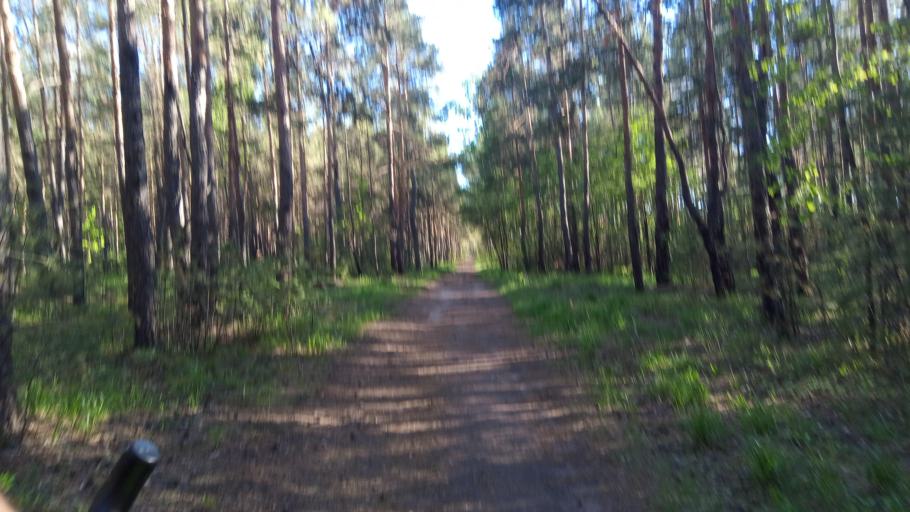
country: RU
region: Chelyabinsk
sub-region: Gorod Chelyabinsk
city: Chelyabinsk
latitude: 55.1364
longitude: 61.3364
